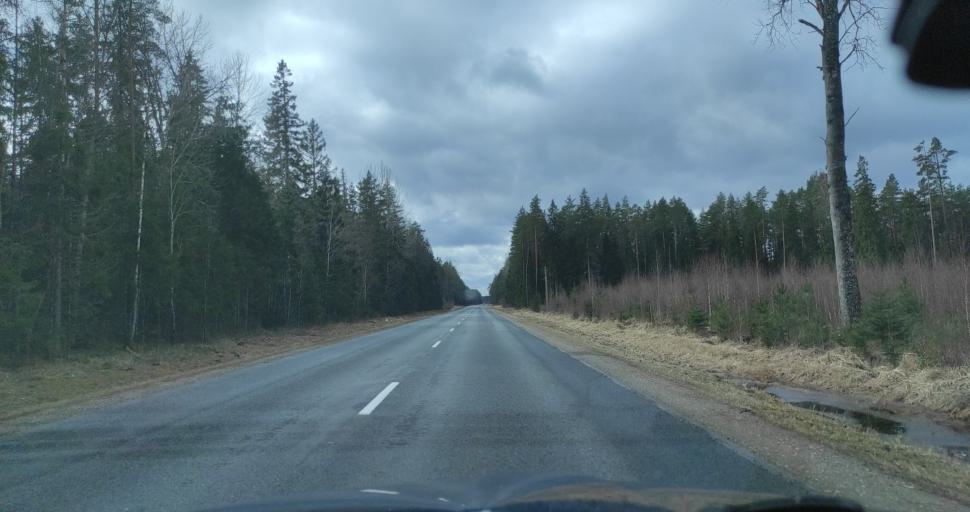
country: LV
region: Talsu Rajons
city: Stende
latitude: 57.1161
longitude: 22.5123
